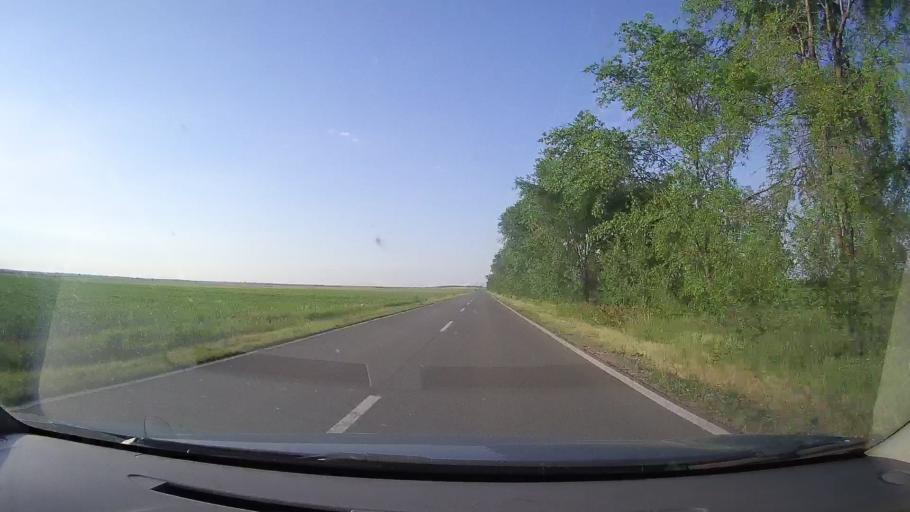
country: RS
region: Autonomna Pokrajina Vojvodina
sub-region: Juznobanatski Okrug
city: Vrsac
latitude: 45.1803
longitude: 21.2957
